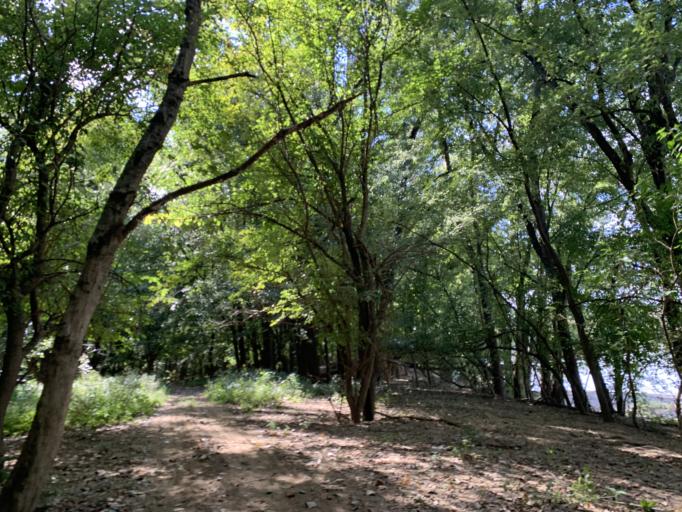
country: US
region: Indiana
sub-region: Floyd County
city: New Albany
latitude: 38.2772
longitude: -85.8183
